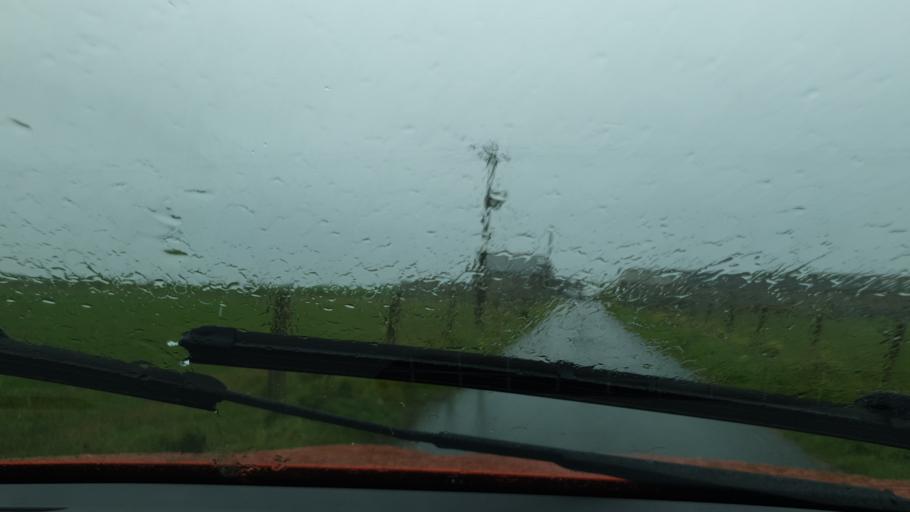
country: GB
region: England
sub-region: Cumbria
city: Barrow in Furness
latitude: 54.0568
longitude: -3.2143
